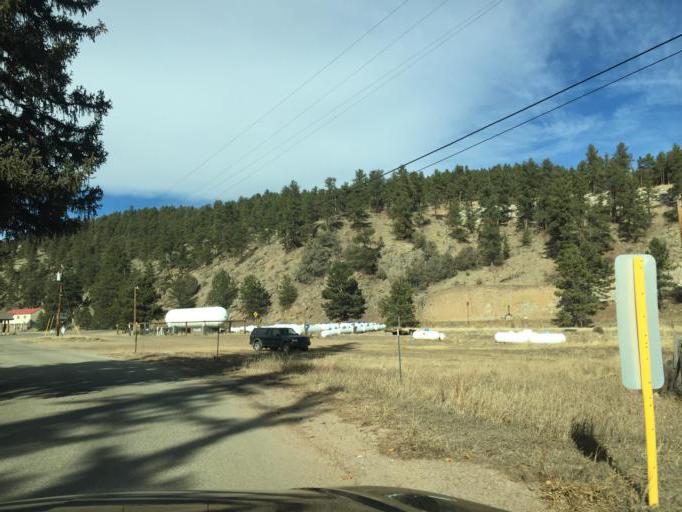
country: US
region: Colorado
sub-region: Jefferson County
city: Evergreen
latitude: 39.4062
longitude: -105.4862
